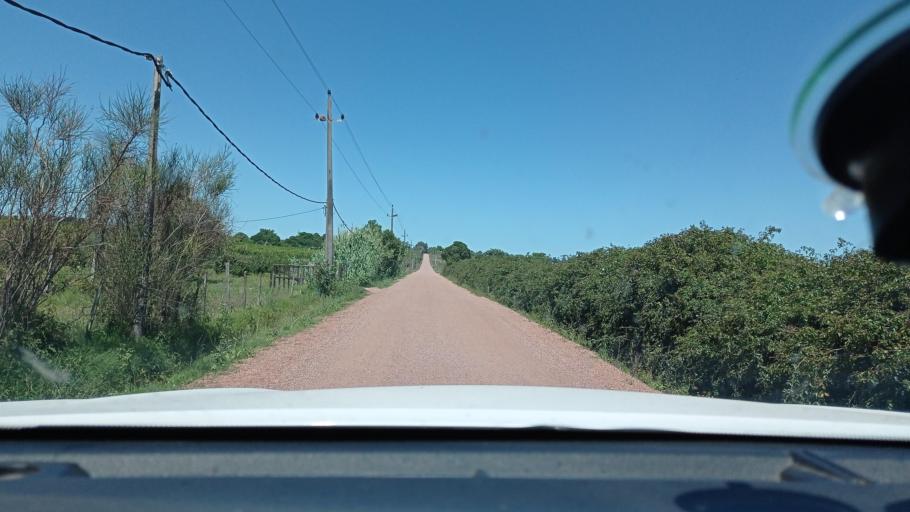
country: UY
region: Canelones
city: La Paz
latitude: -34.7459
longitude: -56.2053
